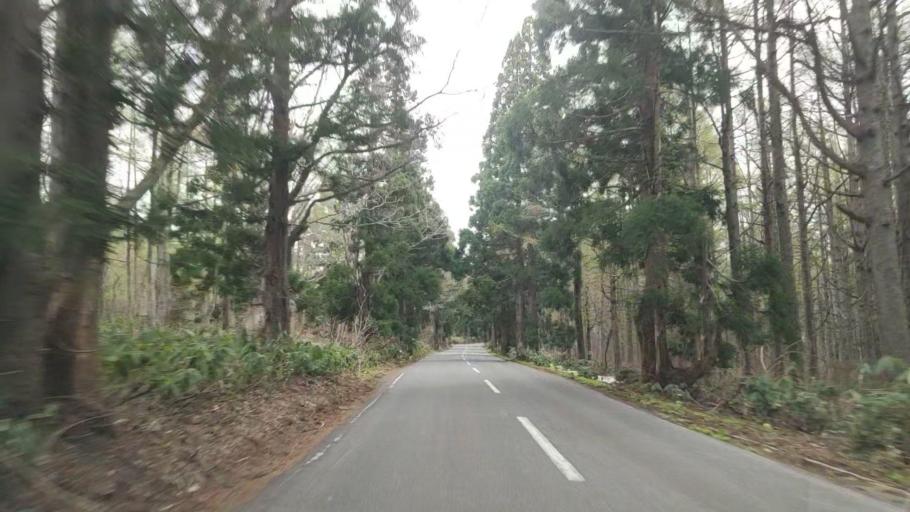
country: JP
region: Aomori
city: Aomori Shi
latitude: 40.7229
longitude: 140.8541
